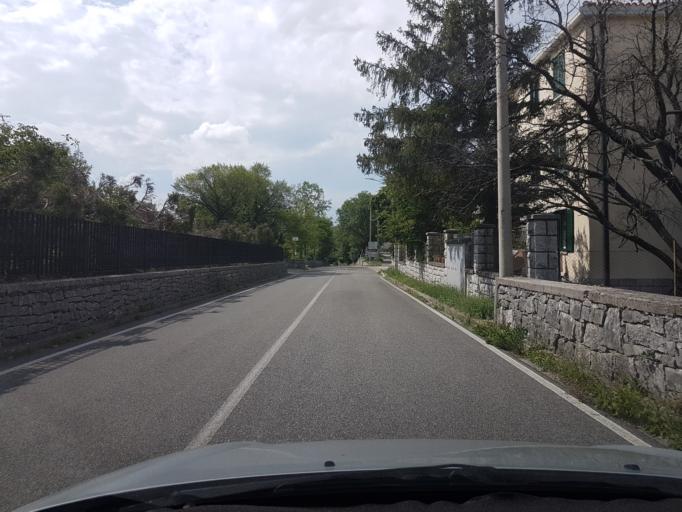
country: IT
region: Friuli Venezia Giulia
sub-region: Provincia di Trieste
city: Zolla
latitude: 45.7177
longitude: 13.8020
